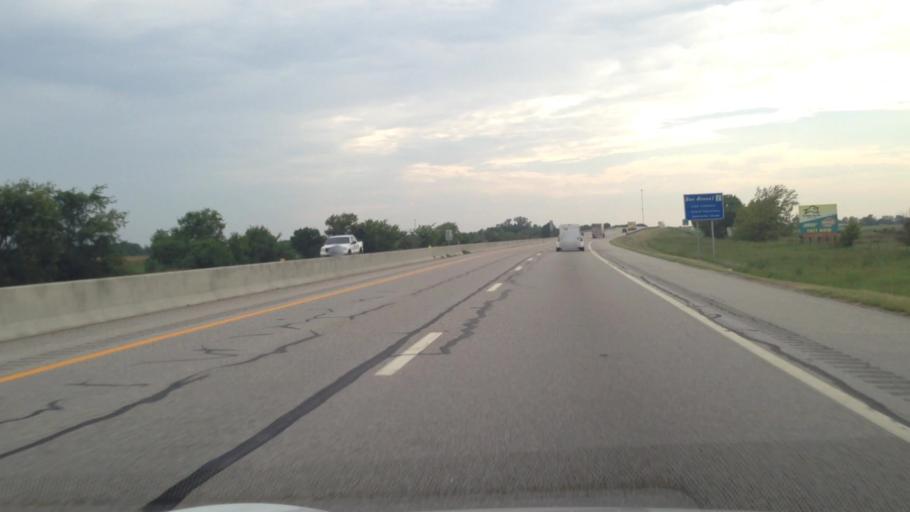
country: US
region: Oklahoma
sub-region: Ottawa County
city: Afton
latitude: 36.7281
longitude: -94.9210
